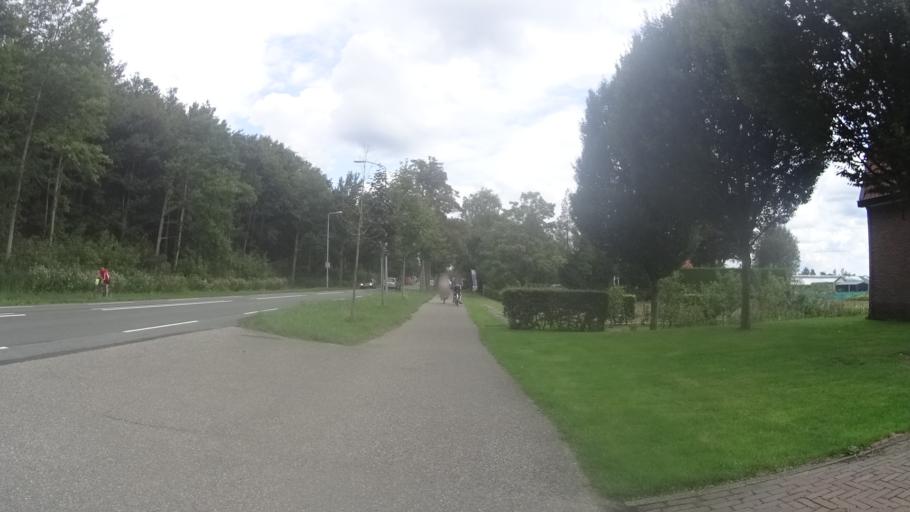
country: NL
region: North Holland
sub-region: Gemeente Castricum
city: Castricum
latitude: 52.5348
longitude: 4.6562
